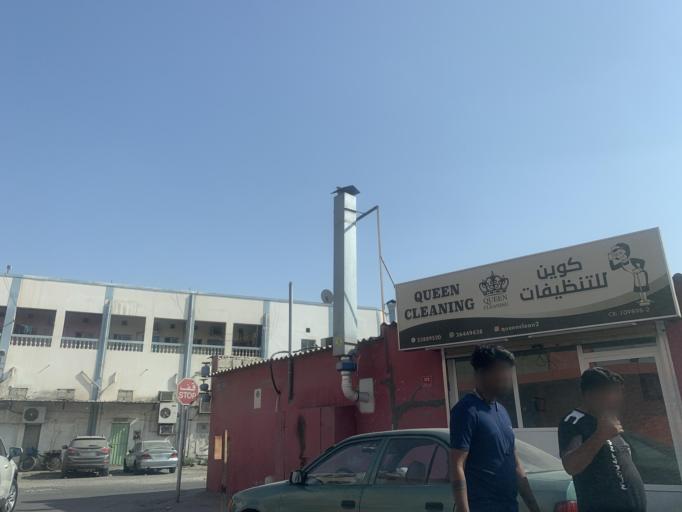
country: BH
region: Central Governorate
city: Madinat Hamad
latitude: 26.1408
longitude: 50.4956
